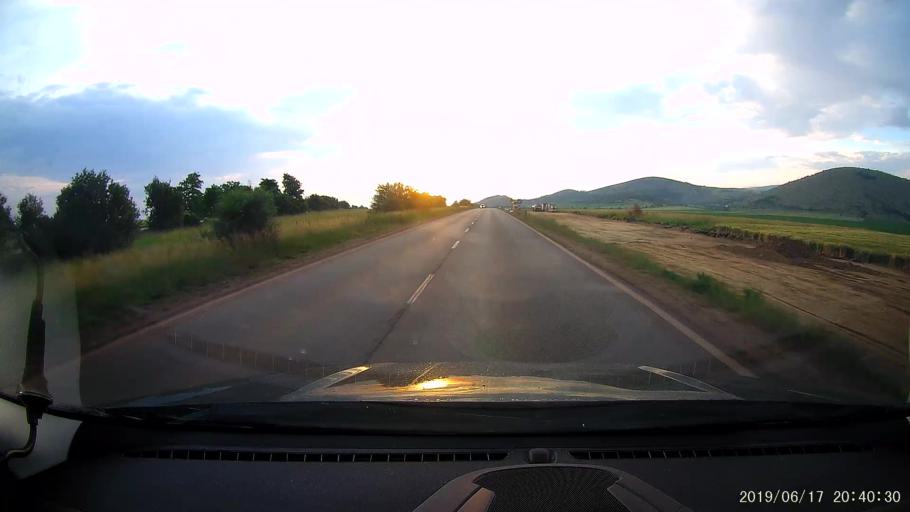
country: BG
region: Sofiya
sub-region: Obshtina Slivnitsa
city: Slivnitsa
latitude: 42.8874
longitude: 22.9853
